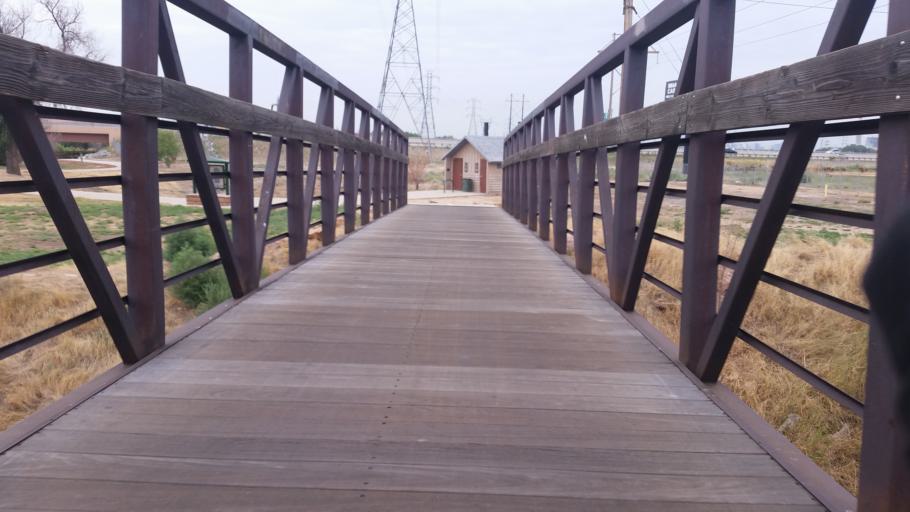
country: US
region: Colorado
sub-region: Adams County
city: Welby
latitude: 39.8275
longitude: -104.9501
